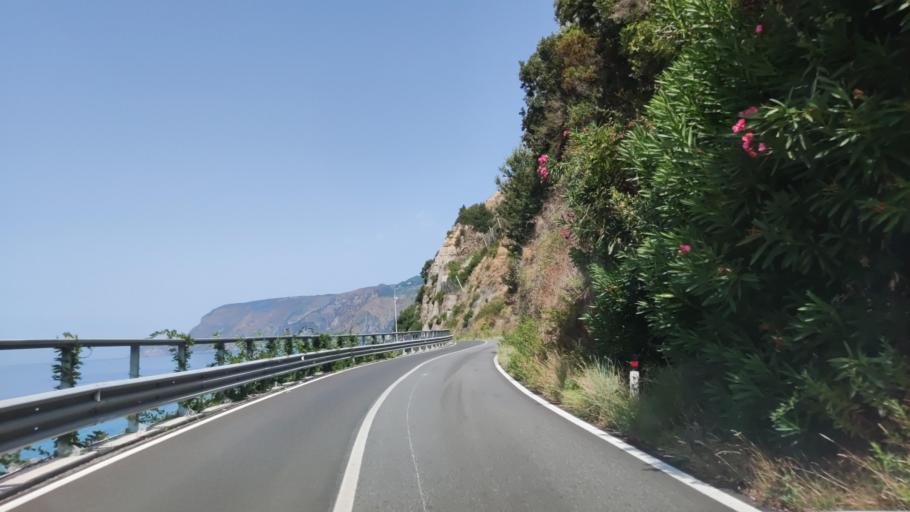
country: IT
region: Calabria
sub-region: Provincia di Reggio Calabria
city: Bagnara Calabra
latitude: 38.2742
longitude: 15.7845
